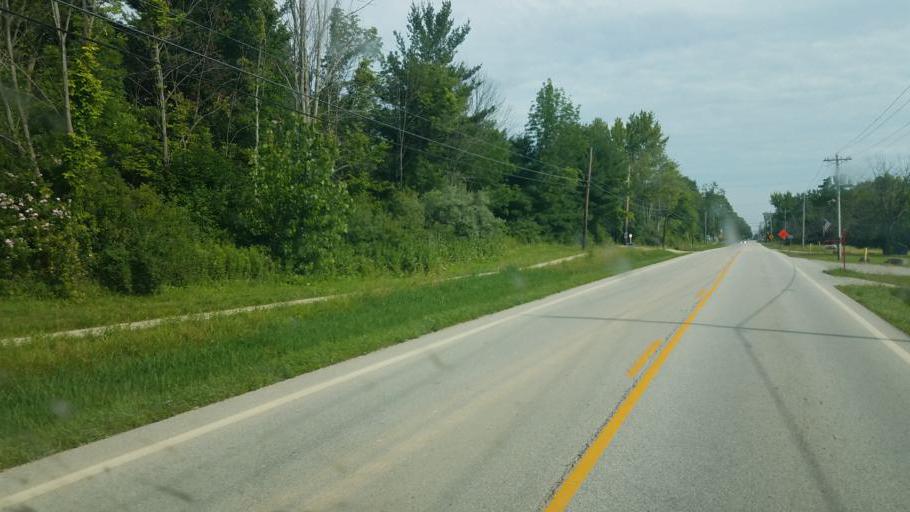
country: US
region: Ohio
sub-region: Medina County
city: Lodi
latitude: 41.0948
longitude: -82.0243
